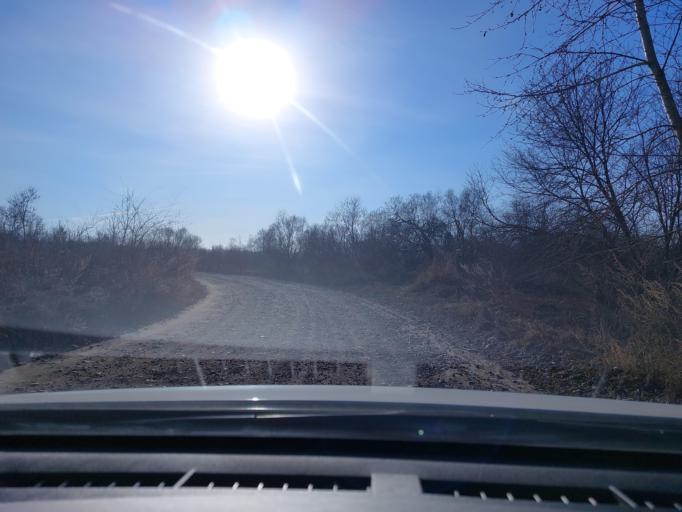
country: RU
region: Irkutsk
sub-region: Irkutskiy Rayon
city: Irkutsk
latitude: 52.3013
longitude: 104.2759
